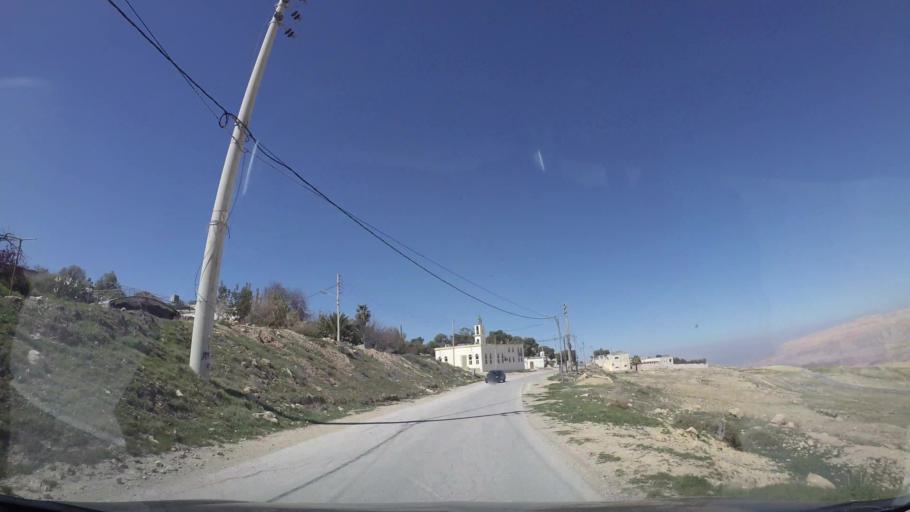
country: JO
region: Tafielah
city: At Tafilah
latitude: 30.8402
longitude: 35.5695
